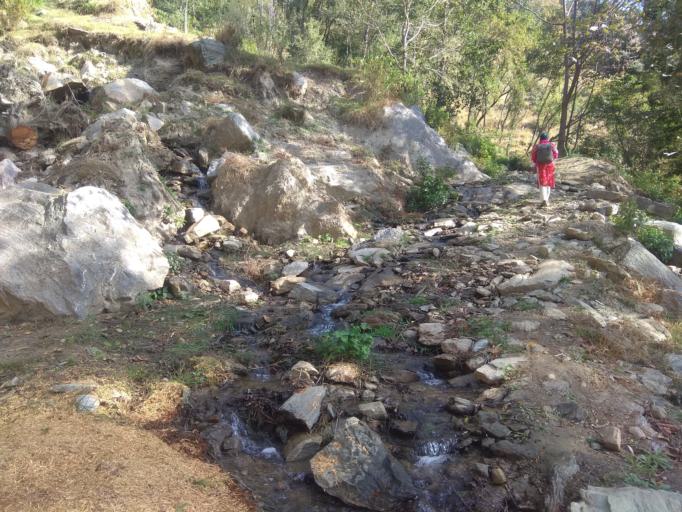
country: NP
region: Mid Western
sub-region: Bheri Zone
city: Dailekh
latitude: 29.2411
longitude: 81.6538
